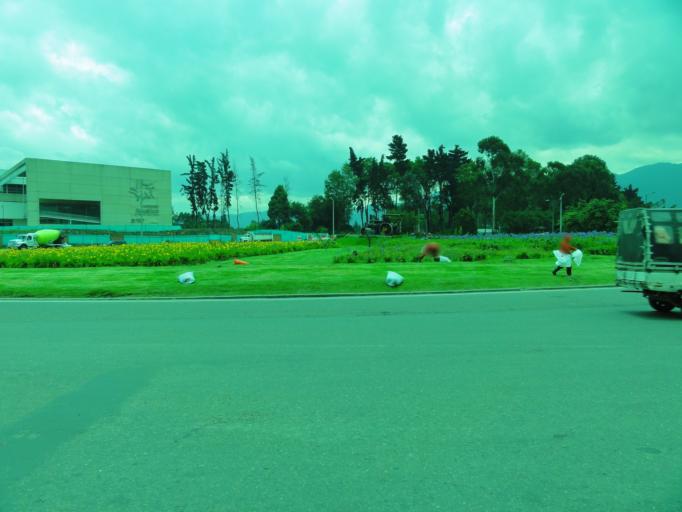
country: CO
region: Bogota D.C.
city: Bogota
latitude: 4.6532
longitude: -74.0840
